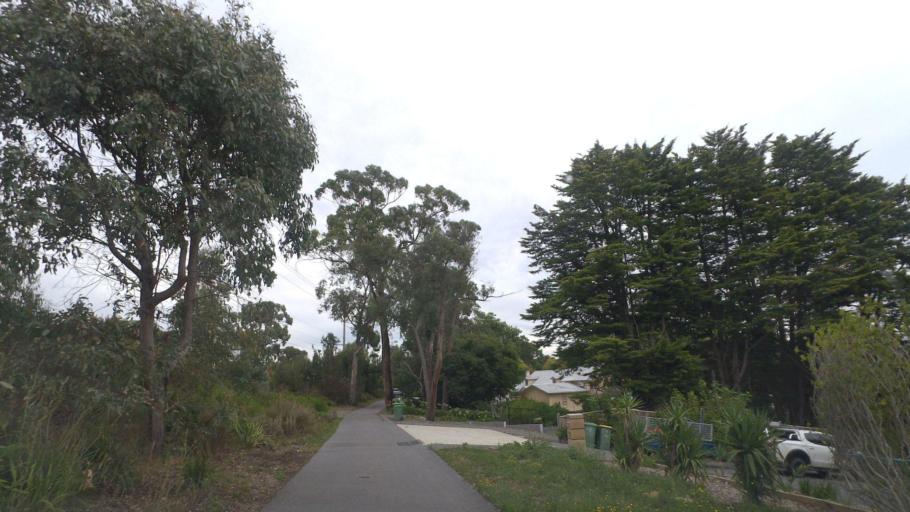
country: AU
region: Victoria
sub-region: Yarra Ranges
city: Kilsyth
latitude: -37.7932
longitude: 145.3349
